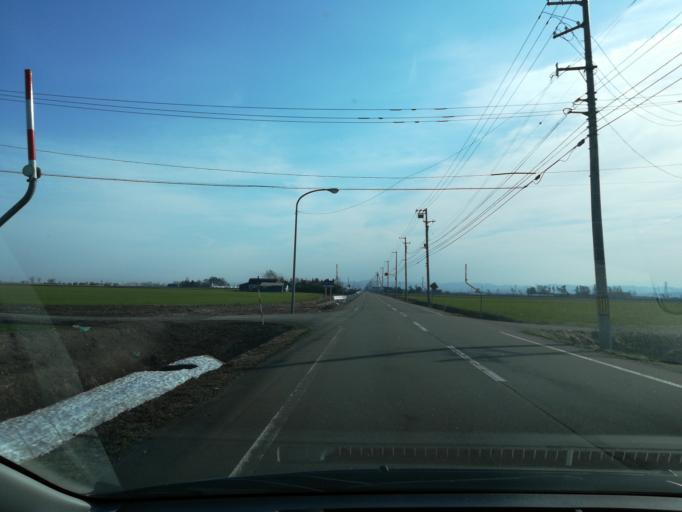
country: JP
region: Hokkaido
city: Iwamizawa
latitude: 43.1687
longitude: 141.6647
